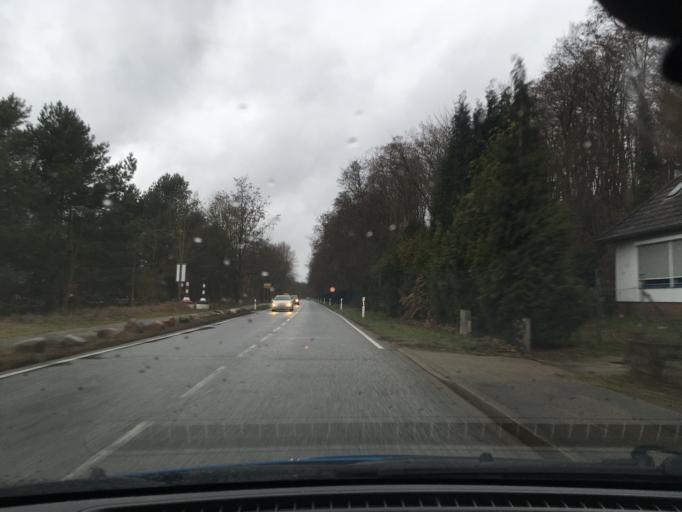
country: DE
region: Lower Saxony
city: Tespe
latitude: 53.4029
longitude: 10.4251
